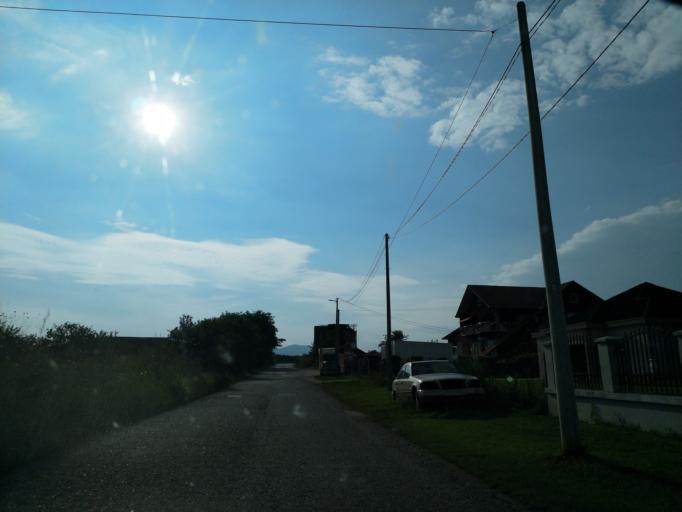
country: RS
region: Central Serbia
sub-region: Pomoravski Okrug
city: Jagodina
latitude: 43.9784
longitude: 21.2330
